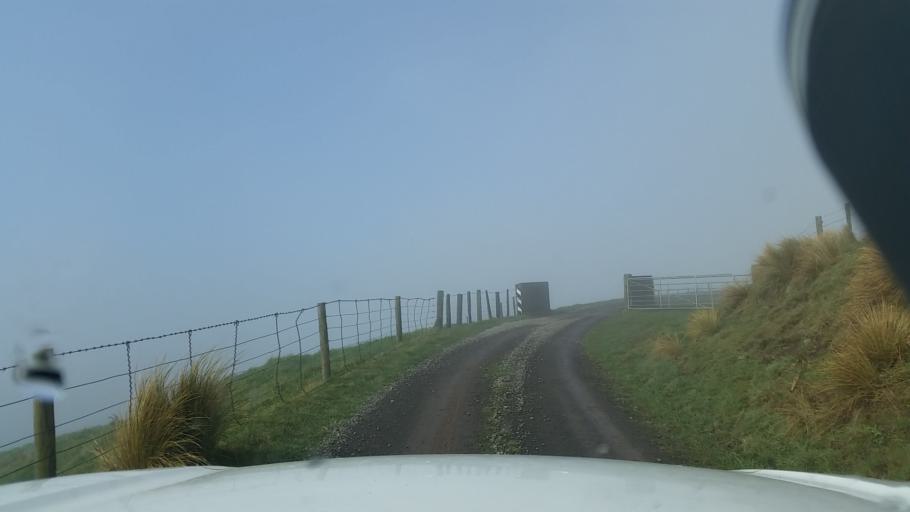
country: NZ
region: Canterbury
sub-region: Christchurch City
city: Christchurch
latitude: -43.6540
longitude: 172.8833
